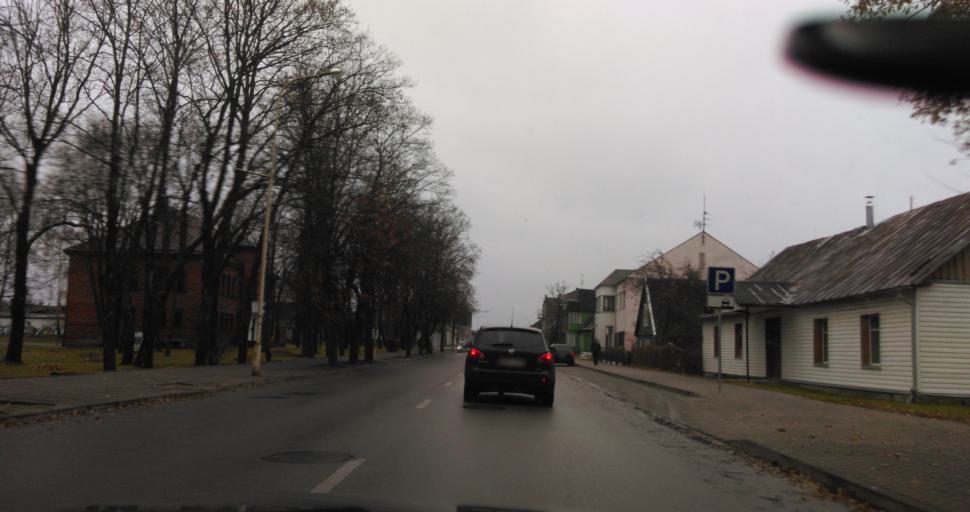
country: LT
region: Panevezys
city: Rokiskis
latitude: 55.9670
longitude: 25.5858
